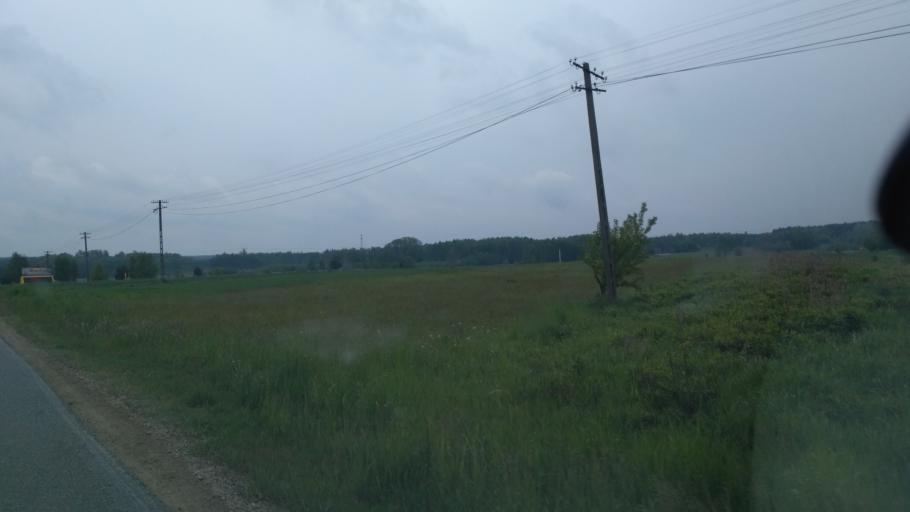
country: PL
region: Subcarpathian Voivodeship
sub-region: Powiat ropczycko-sedziszowski
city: Sedziszow Malopolski
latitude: 50.1032
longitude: 21.7373
